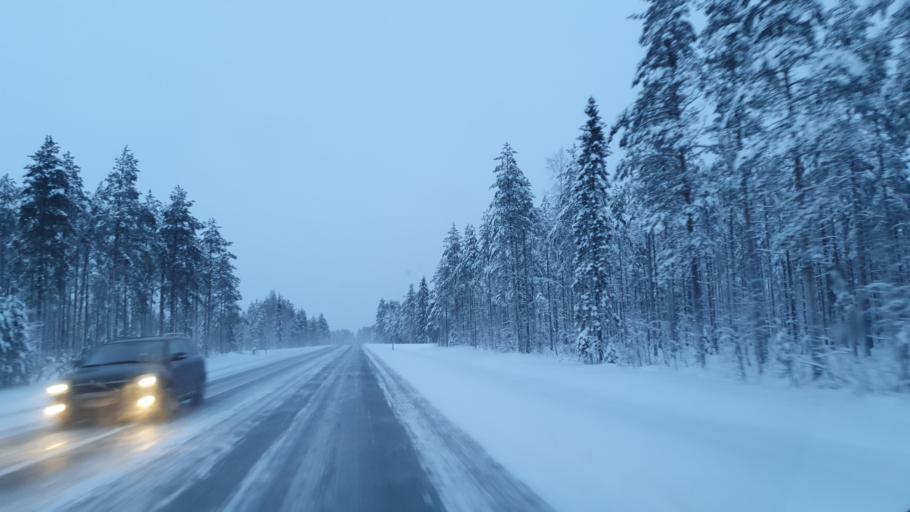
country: FI
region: Northern Ostrobothnia
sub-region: Oulunkaari
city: Utajaervi
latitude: 64.6300
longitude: 26.5919
